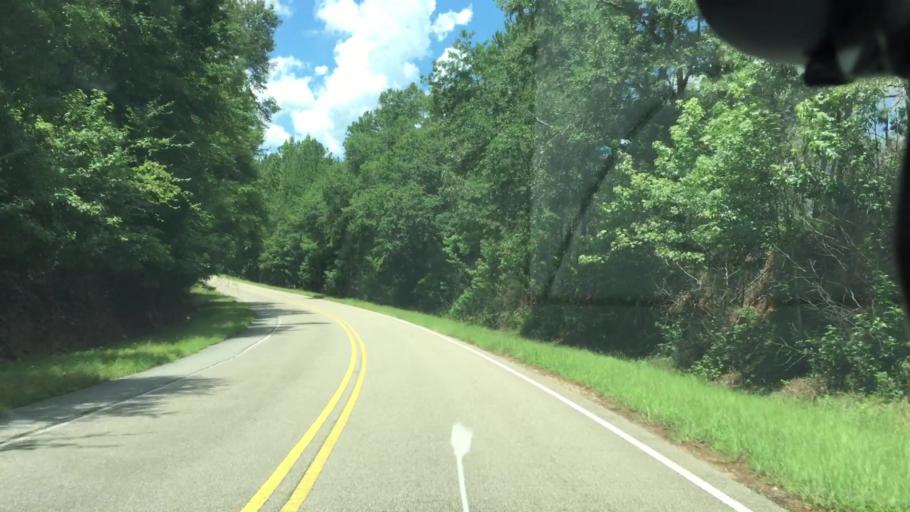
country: US
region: Alabama
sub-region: Coffee County
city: New Brockton
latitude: 31.4085
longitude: -85.8432
